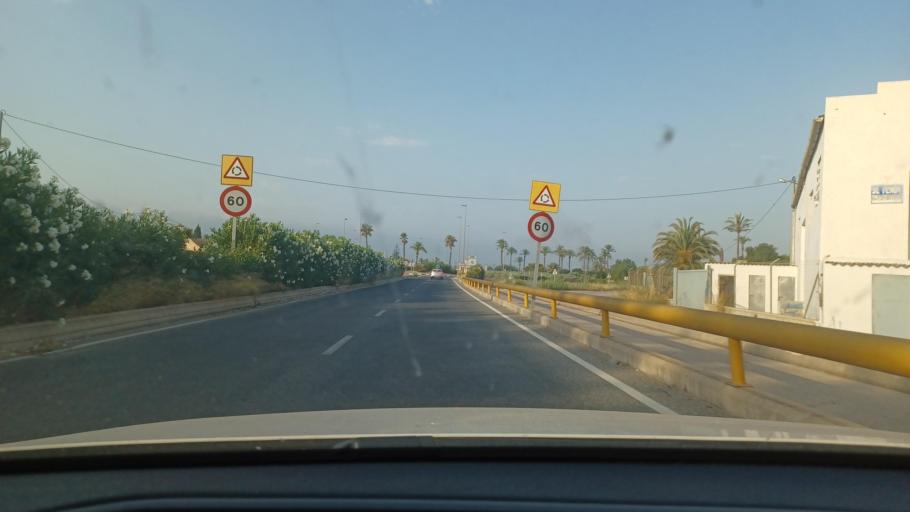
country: ES
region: Valencia
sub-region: Provincia de Alicante
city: Elche
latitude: 38.2069
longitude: -0.6986
